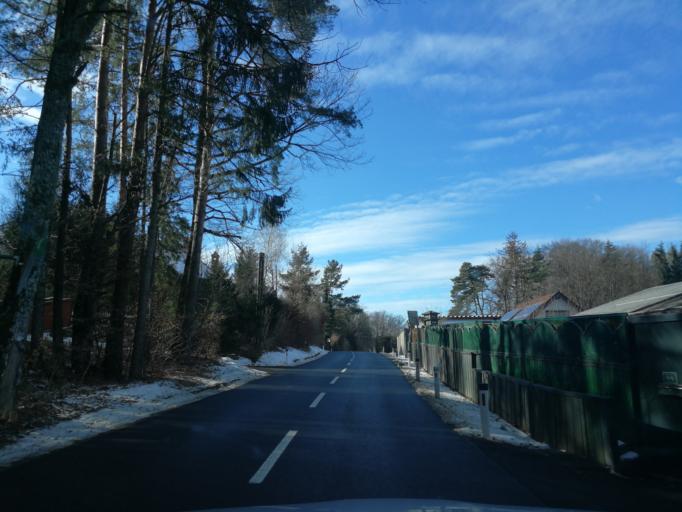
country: AT
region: Styria
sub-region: Politischer Bezirk Graz-Umgebung
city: Langegg bei Graz
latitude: 47.0654
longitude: 15.6384
